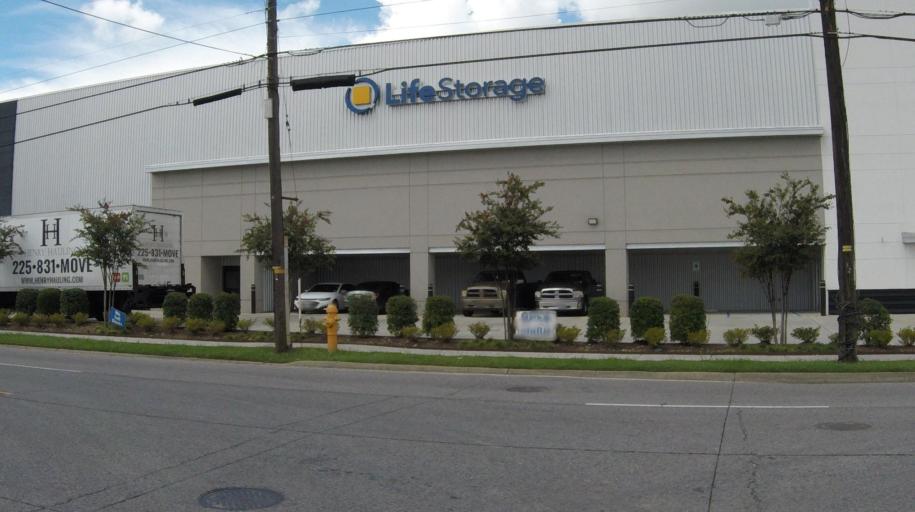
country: US
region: Louisiana
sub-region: West Baton Rouge Parish
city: Port Allen
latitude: 30.4665
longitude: -91.1883
